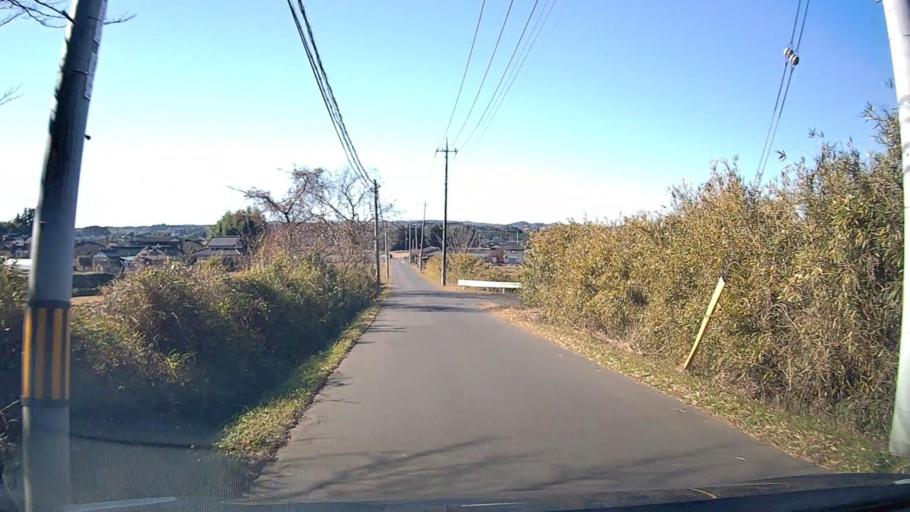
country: JP
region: Ibaraki
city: Mito-shi
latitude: 36.4434
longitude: 140.4365
